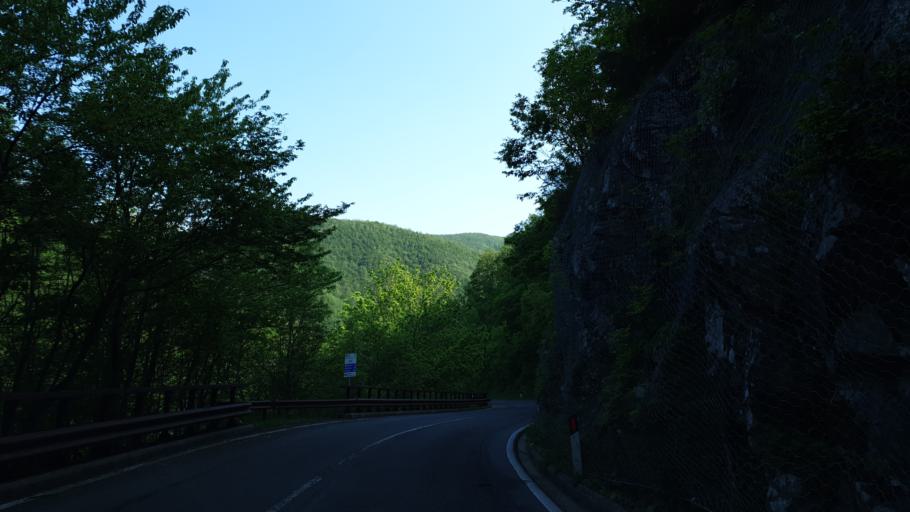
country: IT
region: Tuscany
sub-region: Province of Arezzo
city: Soci
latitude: 43.7782
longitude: 11.8691
